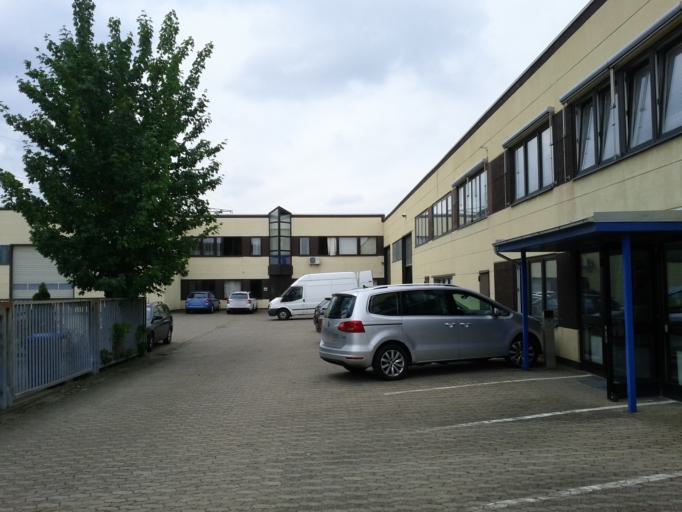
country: DE
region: Lower Saxony
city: Langenhagen
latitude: 52.4321
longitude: 9.6780
